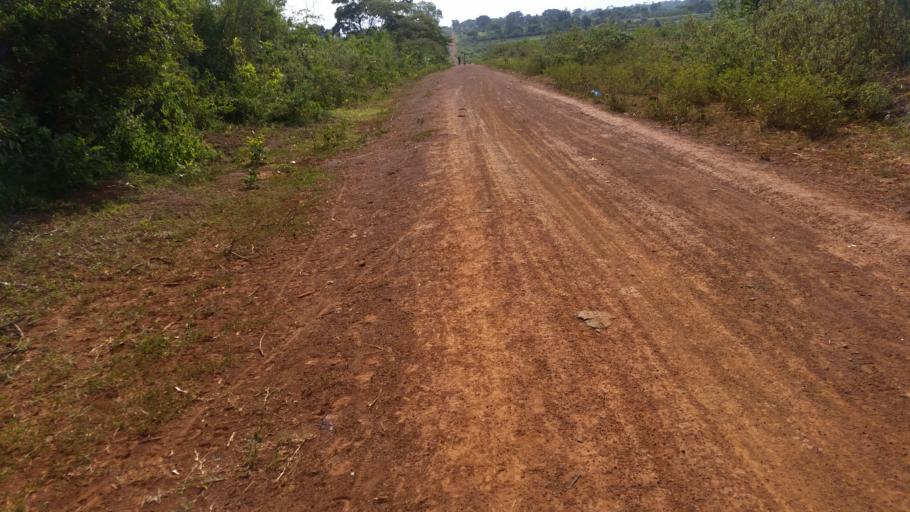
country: UG
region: Eastern Region
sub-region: Busia District
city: Busia
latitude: 0.5490
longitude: 34.0139
